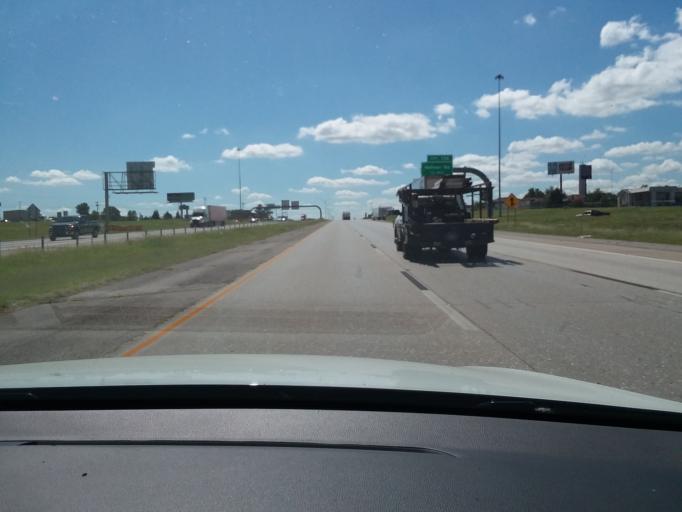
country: US
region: Oklahoma
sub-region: Oklahoma County
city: Edmond
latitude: 35.5928
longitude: -97.4347
